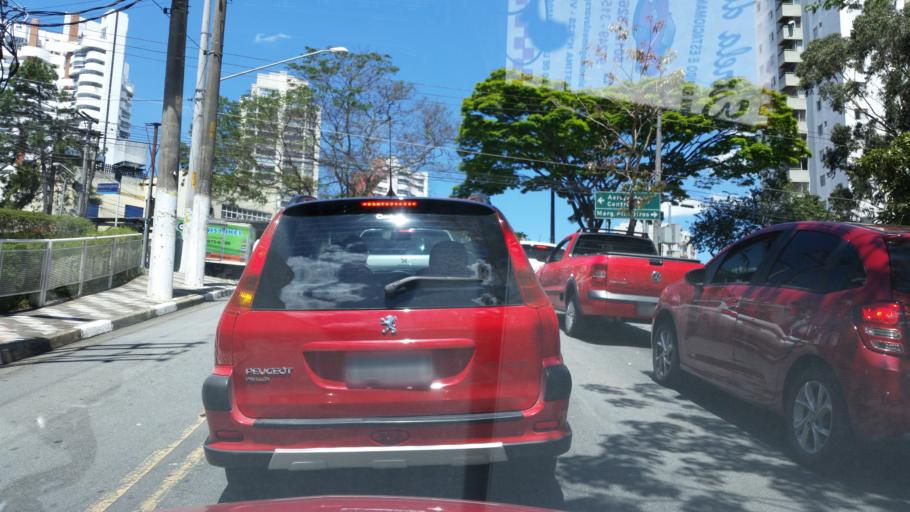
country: BR
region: Sao Paulo
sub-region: Diadema
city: Diadema
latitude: -23.6554
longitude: -46.6930
